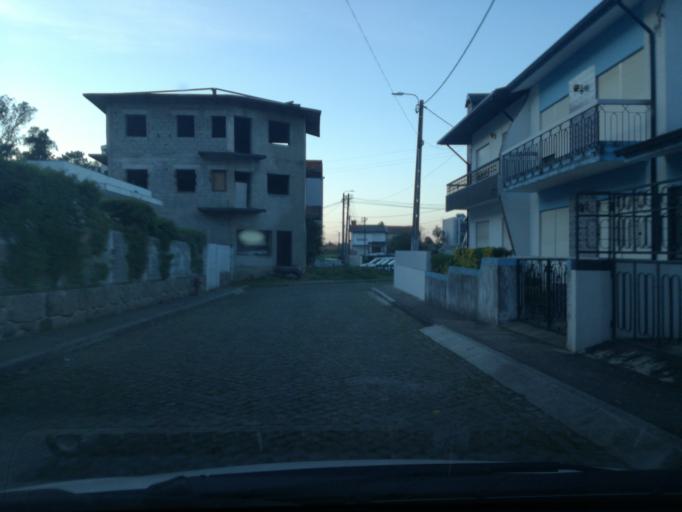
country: PT
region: Porto
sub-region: Maia
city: Gemunde
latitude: 41.2656
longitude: -8.6376
